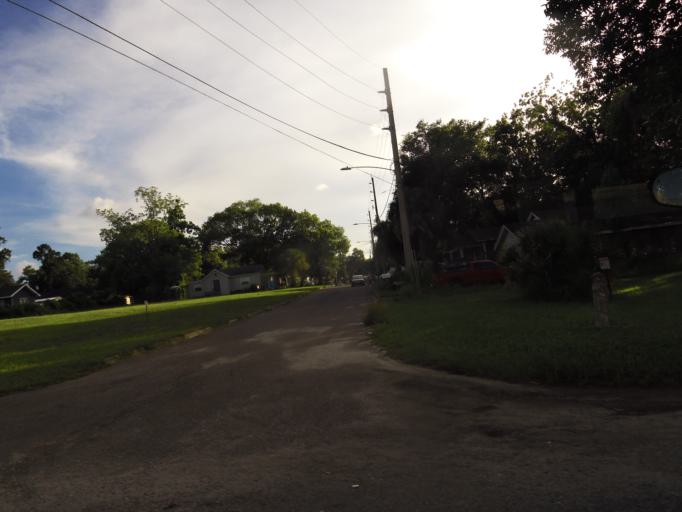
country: US
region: Florida
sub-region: Duval County
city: Jacksonville
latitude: 30.3796
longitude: -81.6659
